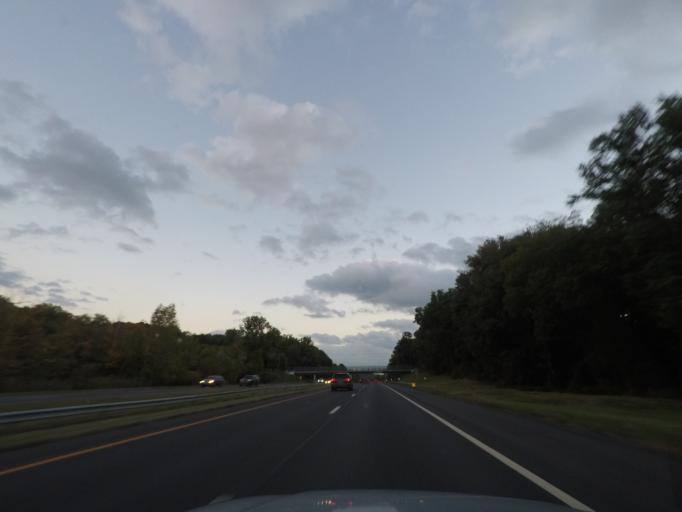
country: US
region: New York
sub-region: Ulster County
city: Tillson
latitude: 41.8328
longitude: -74.0576
